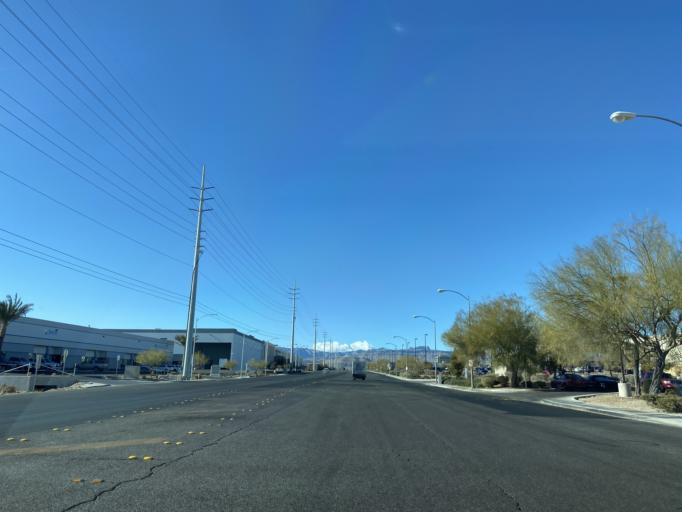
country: US
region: Nevada
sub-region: Clark County
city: Spring Valley
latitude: 36.0709
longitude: -115.2306
